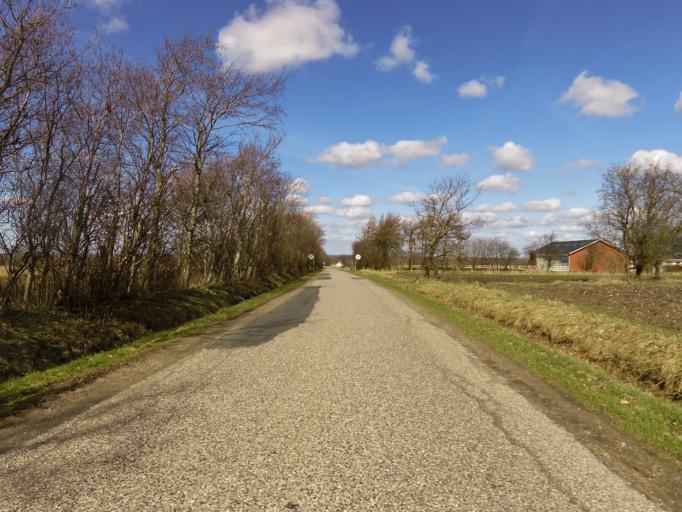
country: DK
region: South Denmark
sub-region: Tonder Kommune
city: Toftlund
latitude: 55.1871
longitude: 9.0951
